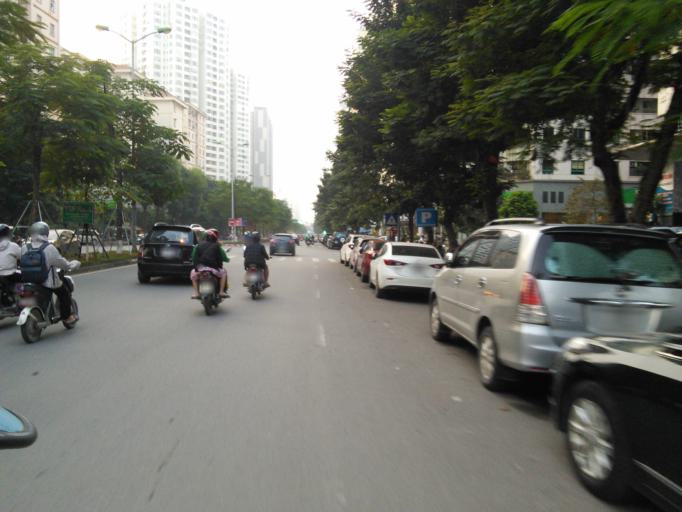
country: VN
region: Ha Noi
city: Thanh Xuan
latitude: 21.0058
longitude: 105.8045
